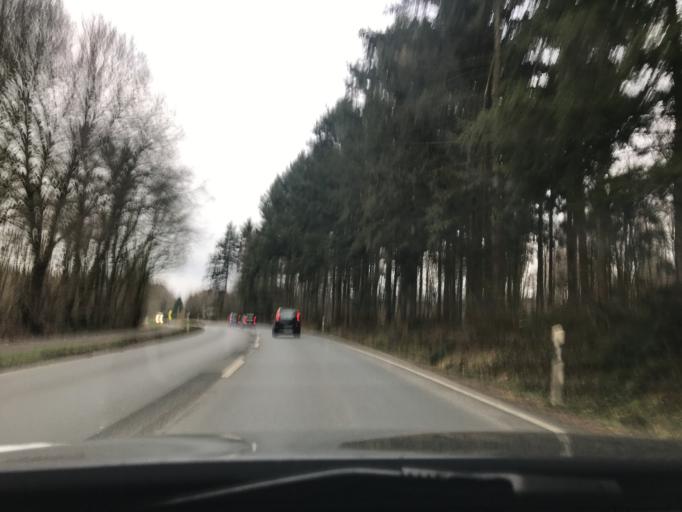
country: DE
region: North Rhine-Westphalia
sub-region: Regierungsbezirk Dusseldorf
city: Kleve
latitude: 51.7707
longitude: 6.1596
